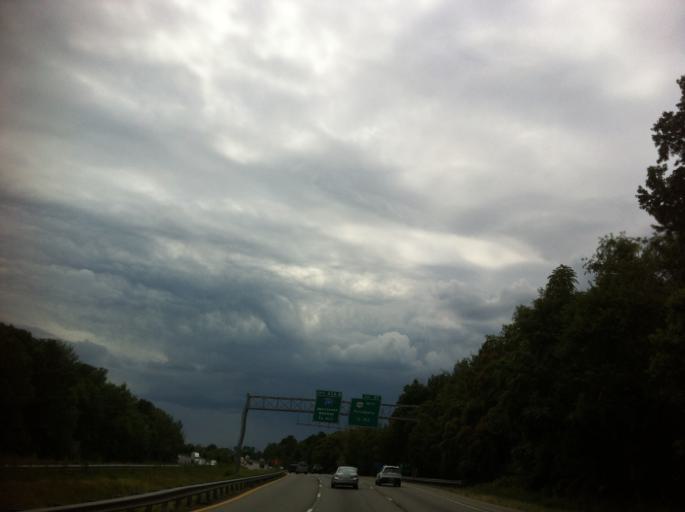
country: US
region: New Jersey
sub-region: Essex County
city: Fairfield
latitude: 40.8762
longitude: -74.3283
